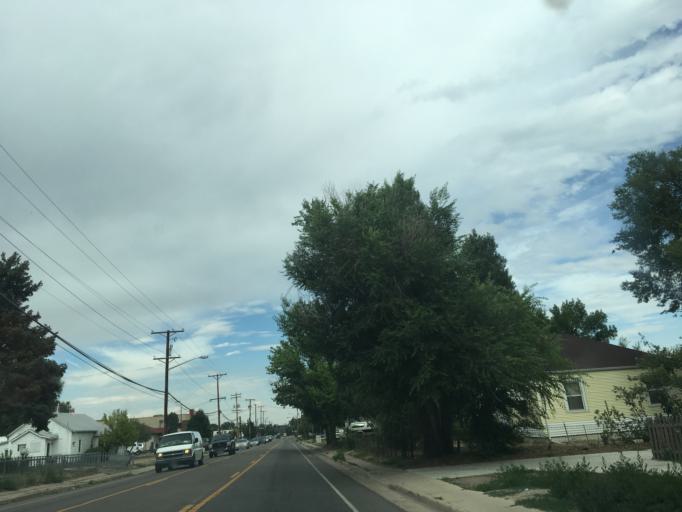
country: US
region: Colorado
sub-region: Arapahoe County
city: Sheridan
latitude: 39.6895
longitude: -105.0293
